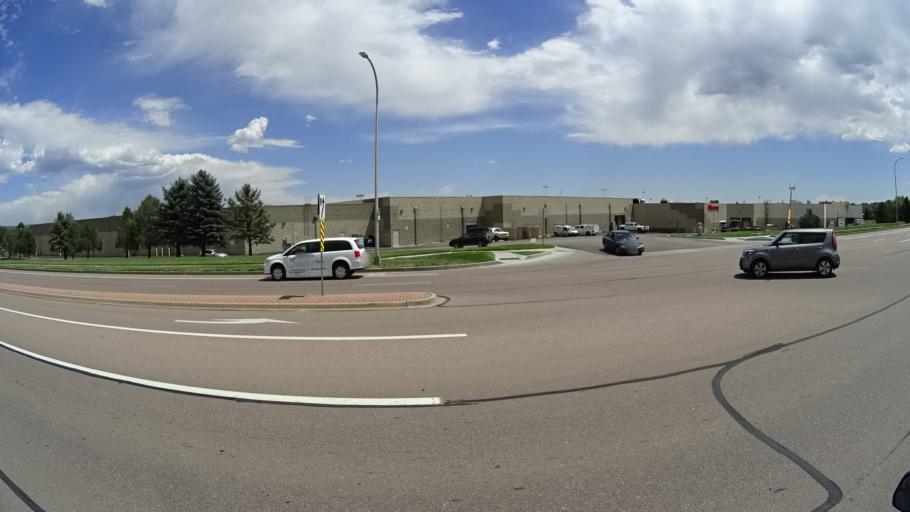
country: US
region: Colorado
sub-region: El Paso County
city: Stratmoor
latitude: 38.7934
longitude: -104.8036
